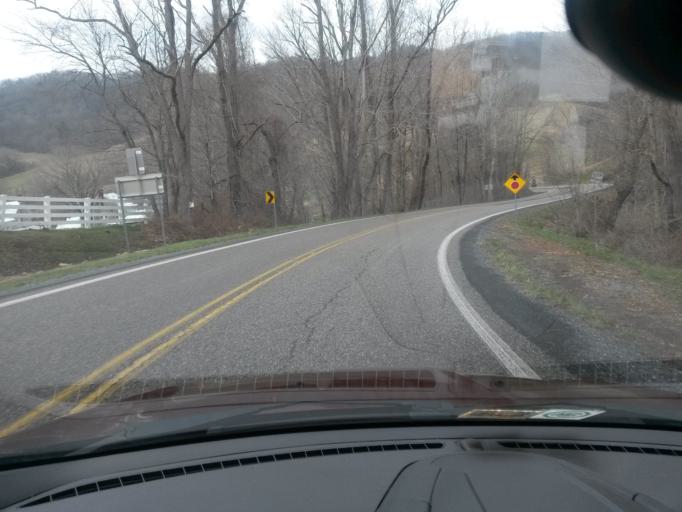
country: US
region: Virginia
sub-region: Bath County
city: Warm Springs
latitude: 38.0529
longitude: -79.7777
